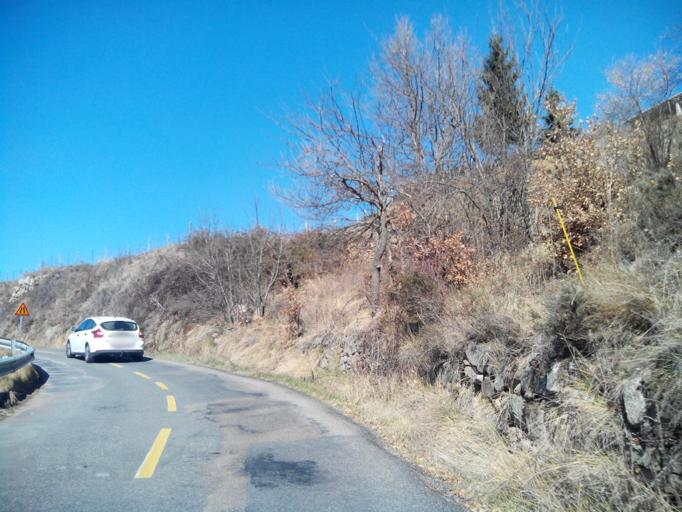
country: ES
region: Catalonia
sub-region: Provincia de Lleida
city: Lles de Cerdanya
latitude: 42.3844
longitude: 1.6812
